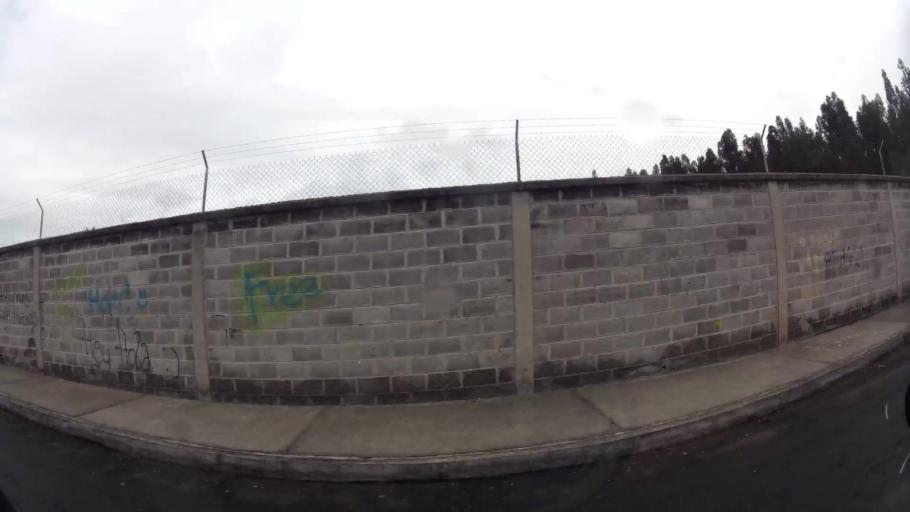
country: EC
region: Pichincha
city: Sangolqui
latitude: -0.2832
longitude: -78.4466
